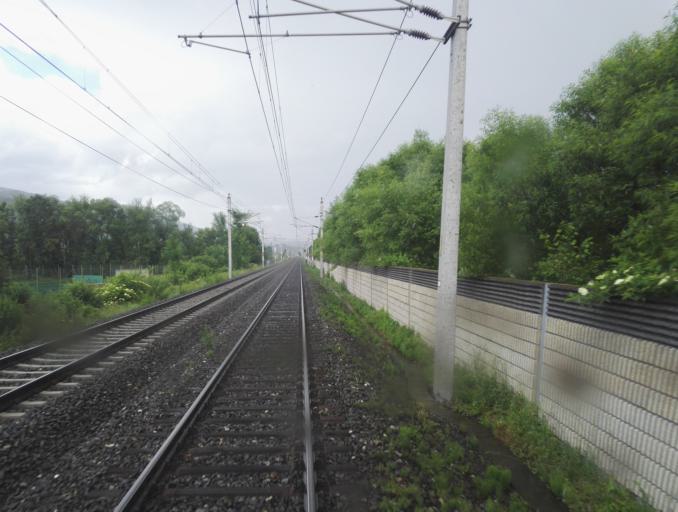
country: AT
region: Styria
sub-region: Politischer Bezirk Bruck-Muerzzuschlag
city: Allerheiligen im Muerztal
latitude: 47.4857
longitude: 15.4095
